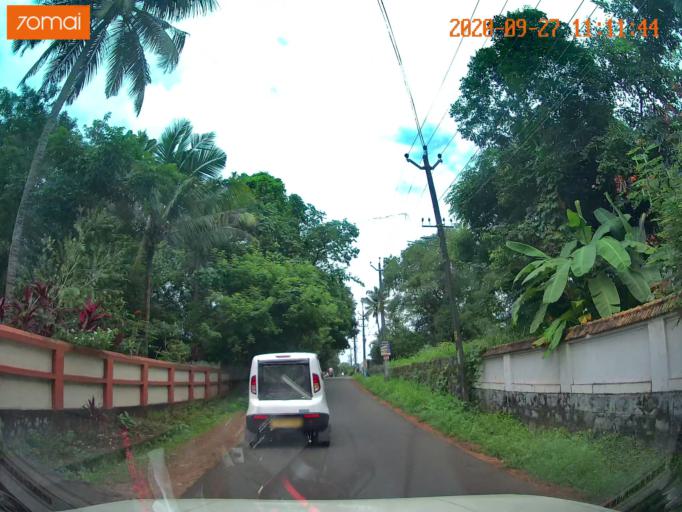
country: IN
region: Kerala
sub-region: Thrissur District
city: Thanniyam
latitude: 10.4323
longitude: 76.2158
